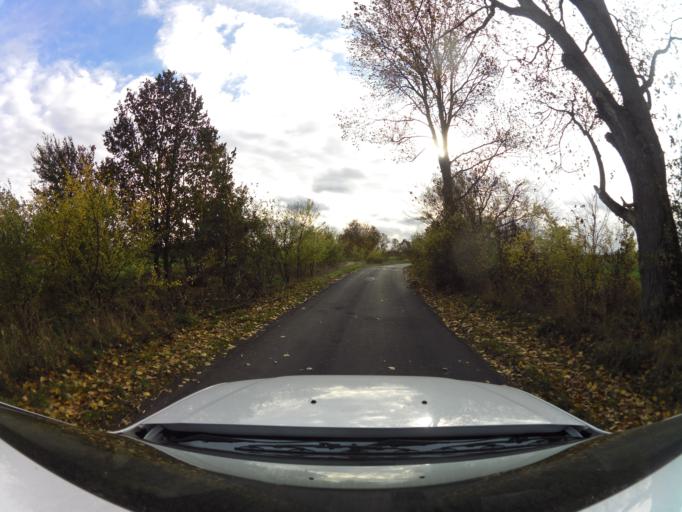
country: PL
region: West Pomeranian Voivodeship
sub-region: Powiat gryficki
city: Gryfice
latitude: 53.8950
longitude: 15.1279
